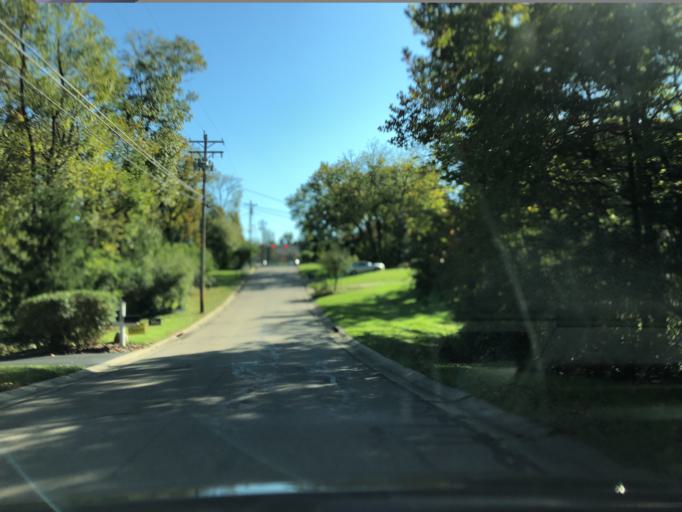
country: US
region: Ohio
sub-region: Hamilton County
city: The Village of Indian Hill
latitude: 39.2630
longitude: -84.2883
